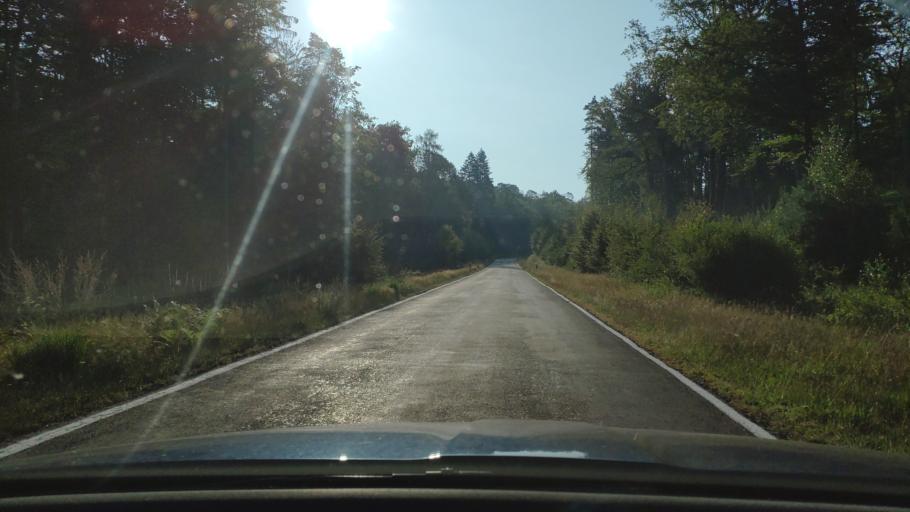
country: DE
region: Rheinland-Pfalz
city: Eppenbrunn
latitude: 49.1113
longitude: 7.5855
